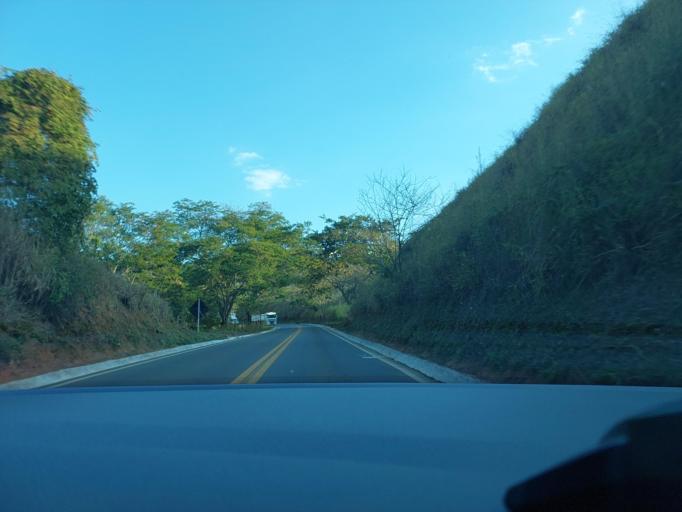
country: BR
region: Minas Gerais
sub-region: Muriae
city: Muriae
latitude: -21.1230
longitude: -42.4034
